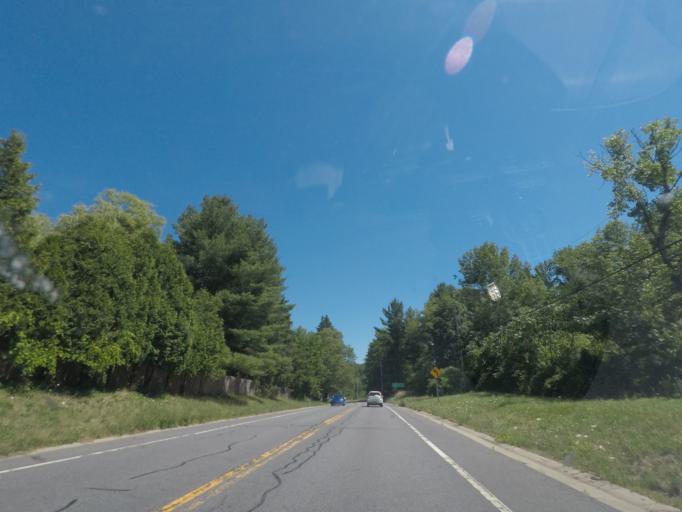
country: US
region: New York
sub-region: Rensselaer County
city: Averill Park
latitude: 42.6541
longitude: -73.5689
